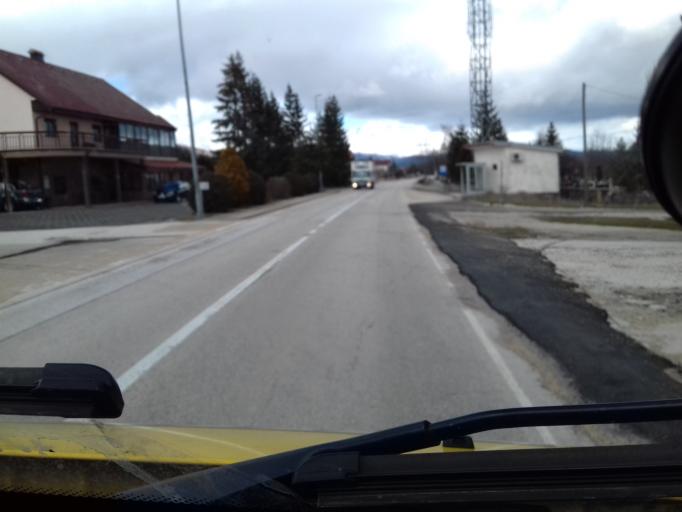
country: BA
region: Federation of Bosnia and Herzegovina
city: Tomislavgrad
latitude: 43.6419
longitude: 17.2319
